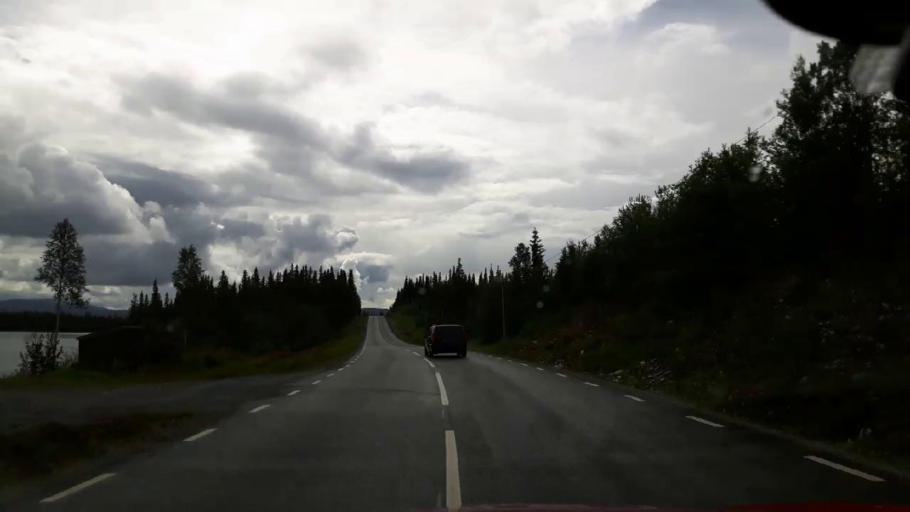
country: NO
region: Nord-Trondelag
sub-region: Royrvik
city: Royrvik
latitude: 64.8384
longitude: 14.1261
